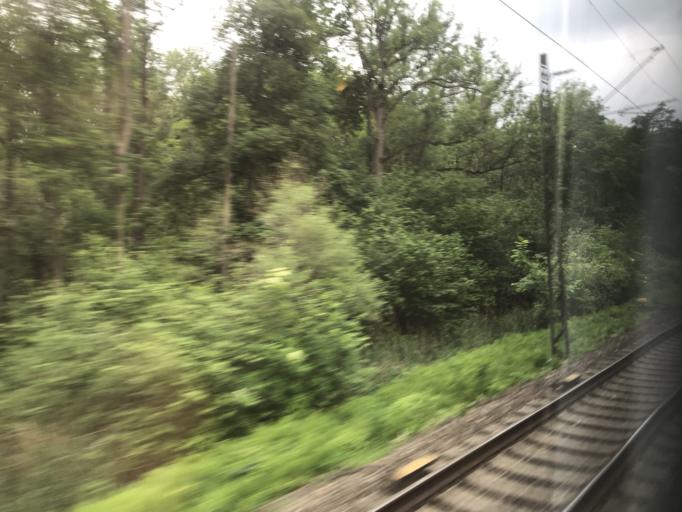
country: DE
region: Bavaria
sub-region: Swabia
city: Bubesheim
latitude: 48.4602
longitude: 10.2499
